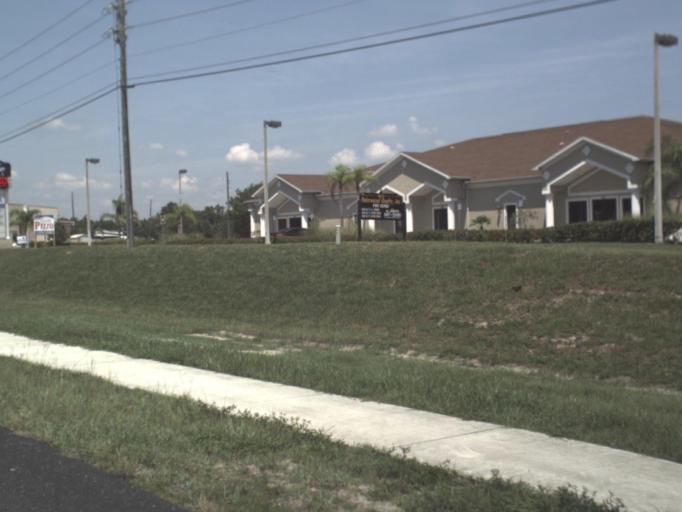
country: US
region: Florida
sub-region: Hernando County
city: Hernando Beach
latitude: 28.4372
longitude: -82.6381
